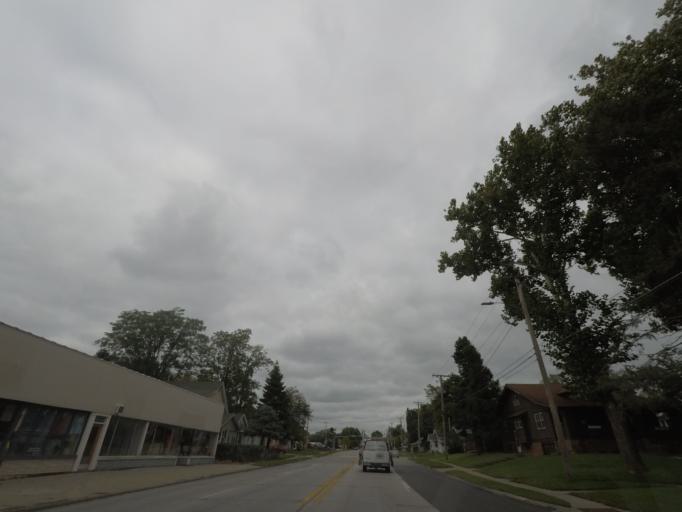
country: US
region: Iowa
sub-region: Polk County
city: Des Moines
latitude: 41.6133
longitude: -93.6005
